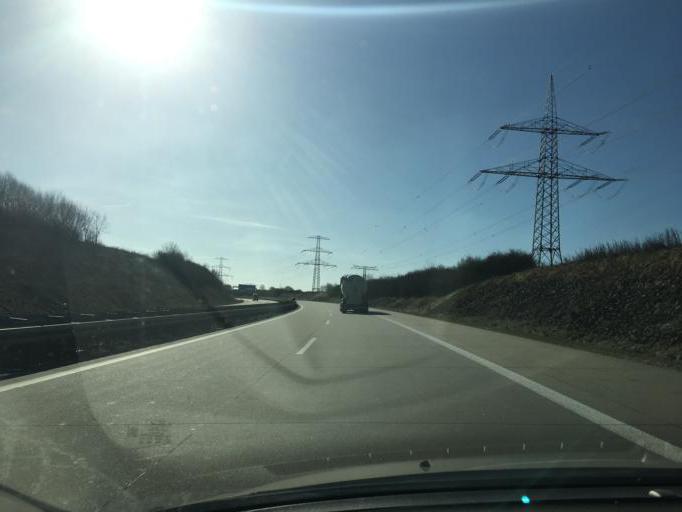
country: DE
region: Saxony
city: Hartmannsdorf
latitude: 50.8706
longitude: 12.7910
